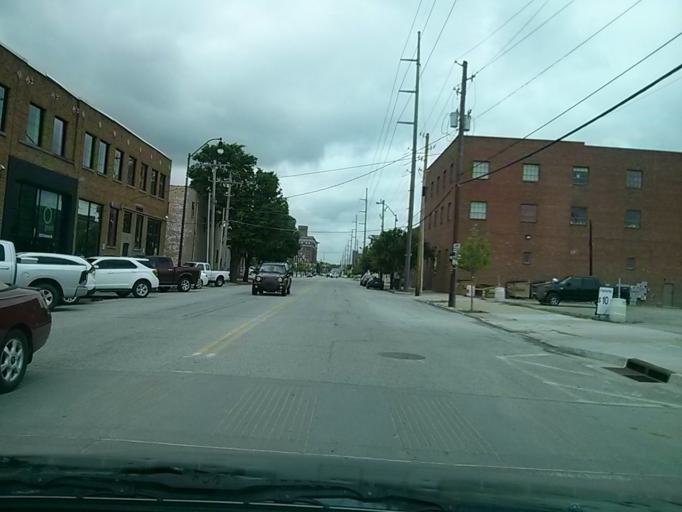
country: US
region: Oklahoma
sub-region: Tulsa County
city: Tulsa
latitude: 36.1590
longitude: -95.9885
